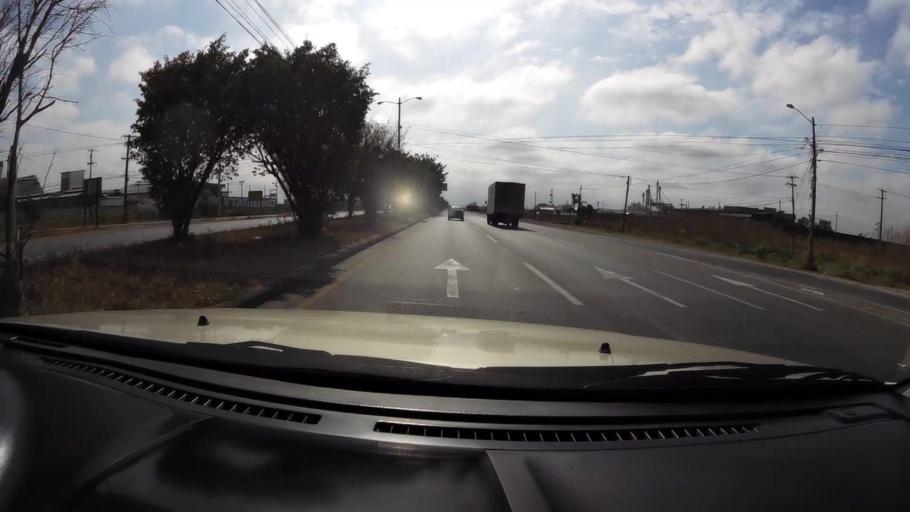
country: EC
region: Guayas
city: Eloy Alfaro
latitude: -2.1858
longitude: -79.8081
